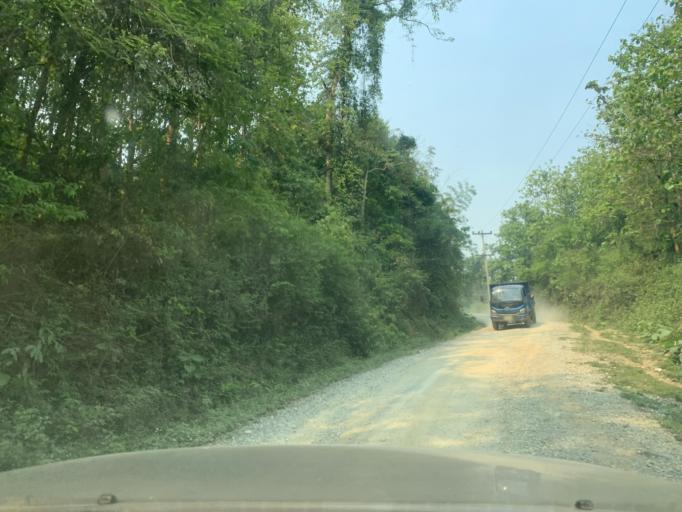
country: LA
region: Louangphabang
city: Louangphabang
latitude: 19.8883
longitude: 102.2514
